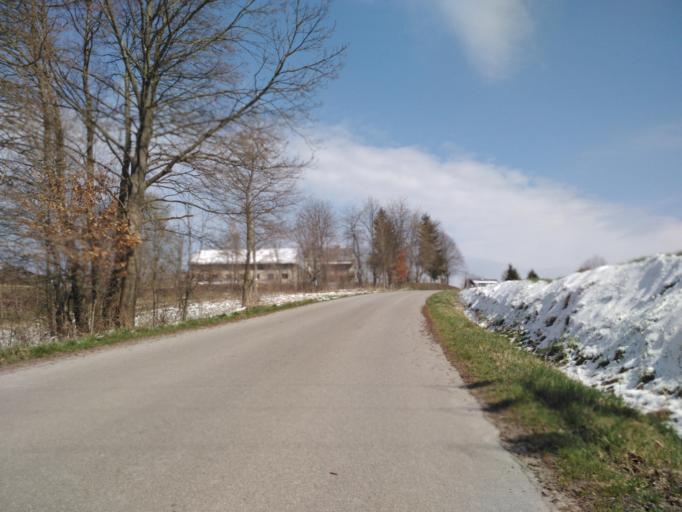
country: PL
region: Subcarpathian Voivodeship
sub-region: Powiat ropczycko-sedziszowski
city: Wielopole Skrzynskie
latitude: 49.9893
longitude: 21.6007
